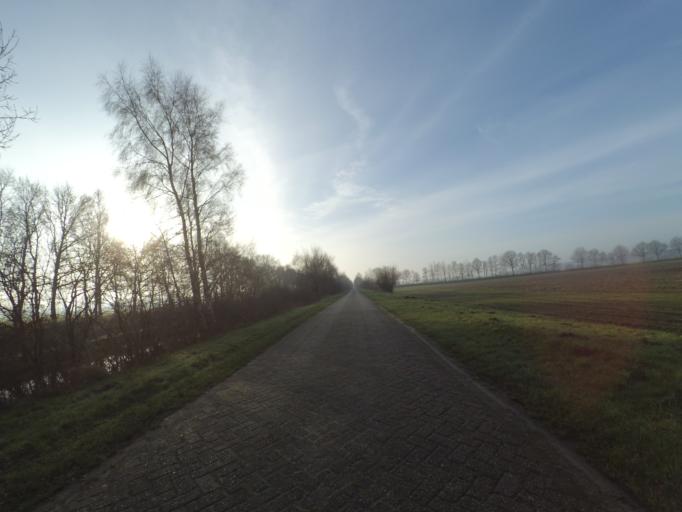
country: NL
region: Drenthe
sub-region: Gemeente Borger-Odoorn
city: Borger
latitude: 52.8905
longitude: 6.7597
